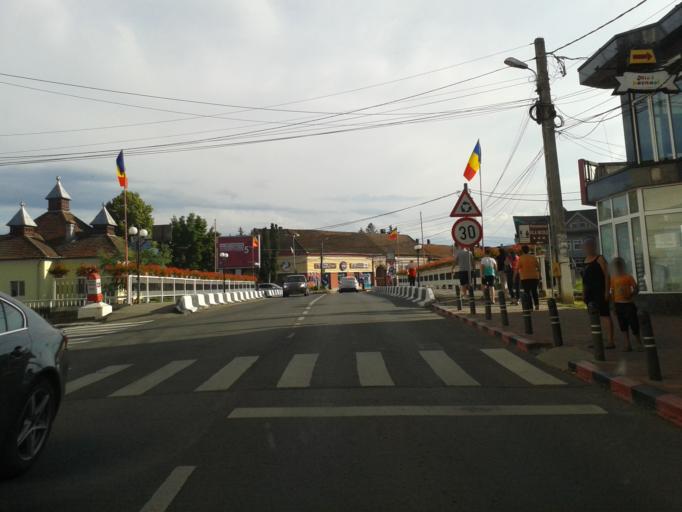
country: RO
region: Hunedoara
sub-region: Oras Hateg
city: Hateg
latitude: 45.6088
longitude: 22.9489
